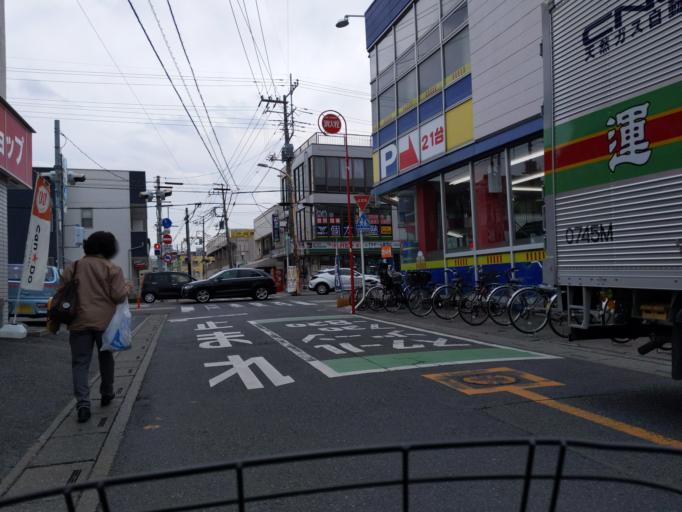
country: JP
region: Saitama
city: Koshigaya
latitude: 35.8529
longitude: 139.7945
